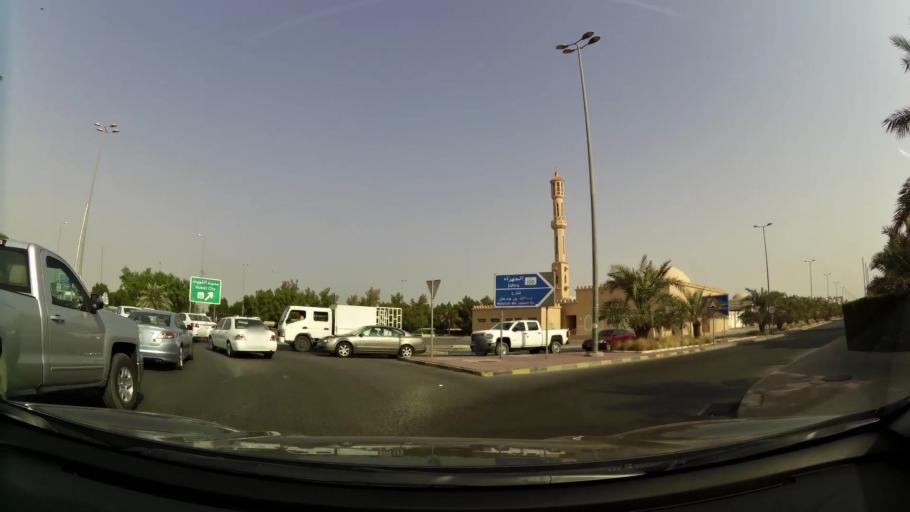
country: KW
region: Muhafazat al Jahra'
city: Al Jahra'
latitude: 29.3601
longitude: 47.6722
